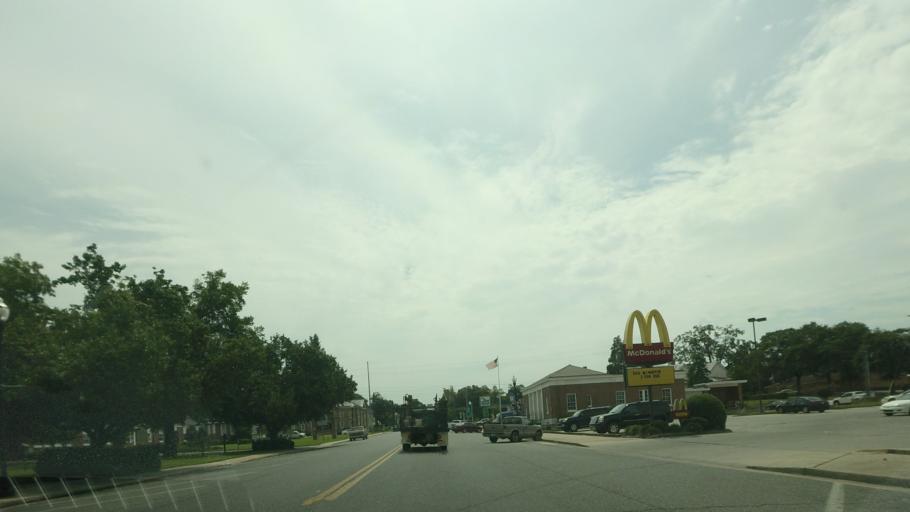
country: US
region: Georgia
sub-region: Bleckley County
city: Cochran
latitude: 32.3873
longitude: -83.3558
